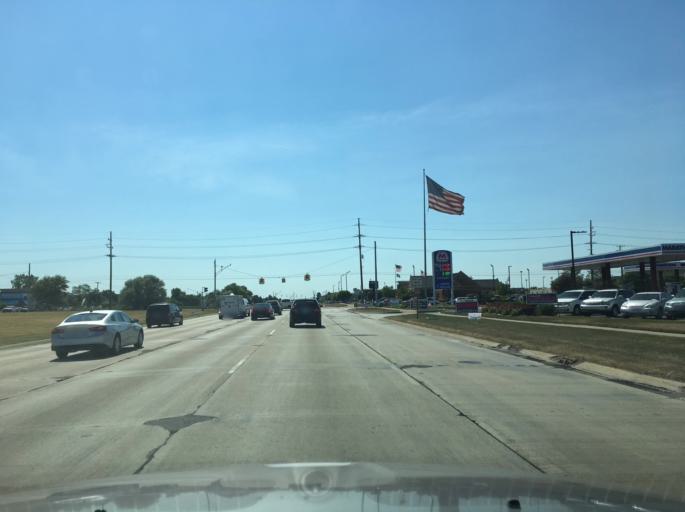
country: US
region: Michigan
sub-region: Macomb County
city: Utica
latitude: 42.6279
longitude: -82.9719
